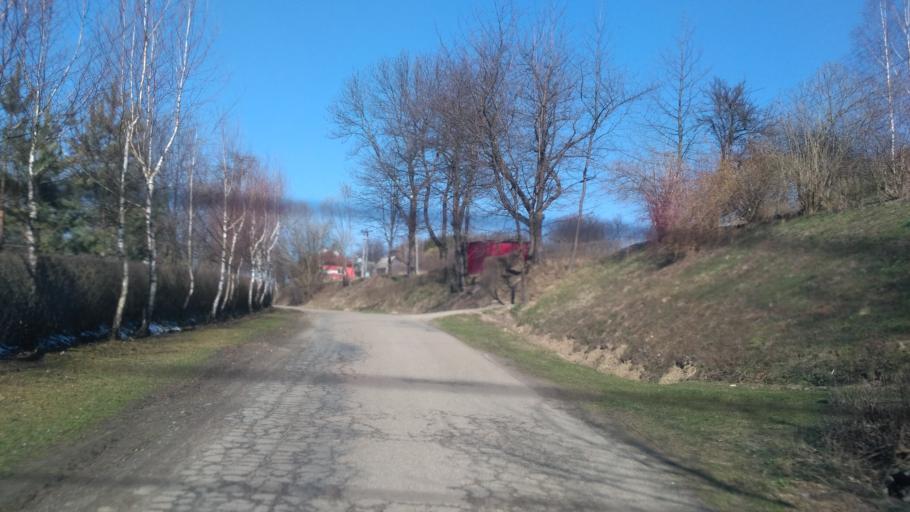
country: PL
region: Subcarpathian Voivodeship
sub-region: Powiat strzyzowski
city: Gwoznica Gorna
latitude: 49.8192
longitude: 22.0174
